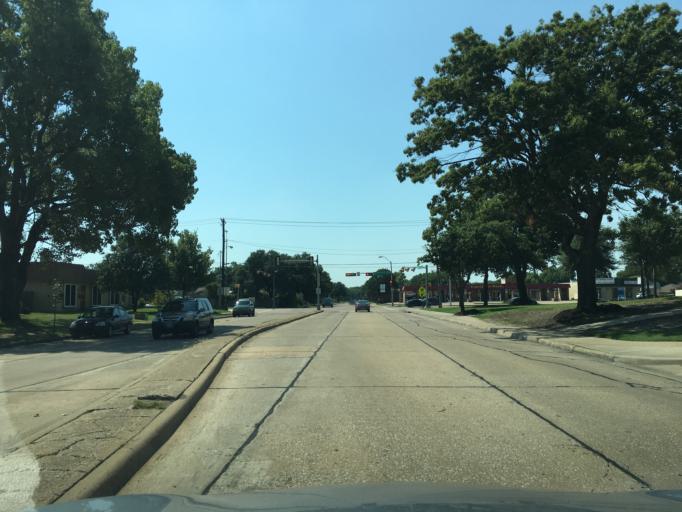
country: US
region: Texas
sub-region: Dallas County
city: Garland
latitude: 32.9317
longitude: -96.6573
